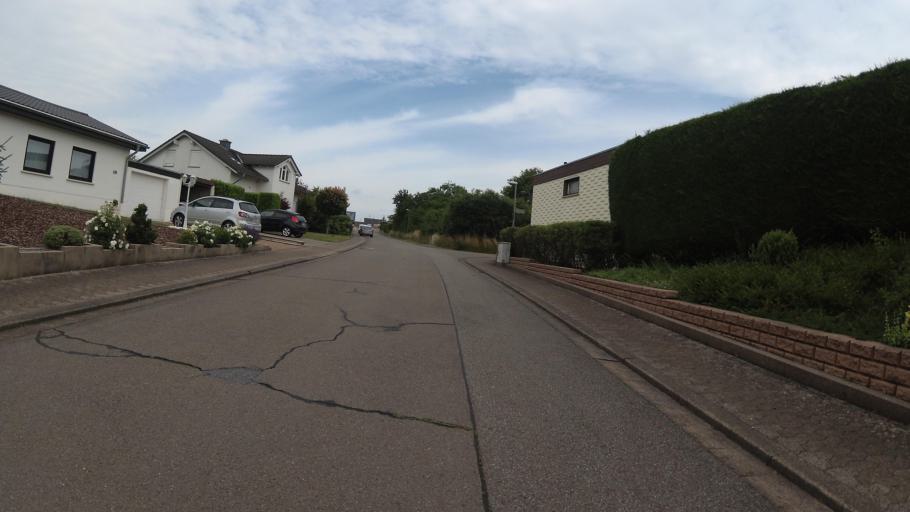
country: DE
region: Saarland
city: Quierschied
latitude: 49.3180
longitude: 7.0433
